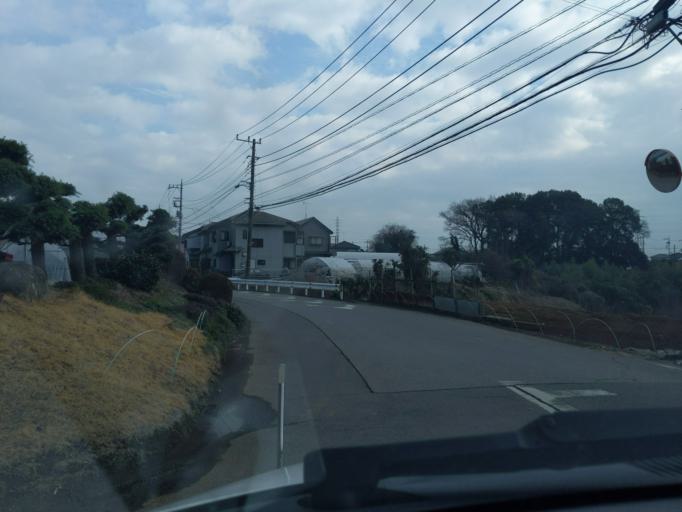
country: JP
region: Saitama
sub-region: Kawaguchi-shi
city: Hatogaya-honcho
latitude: 35.8569
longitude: 139.7211
